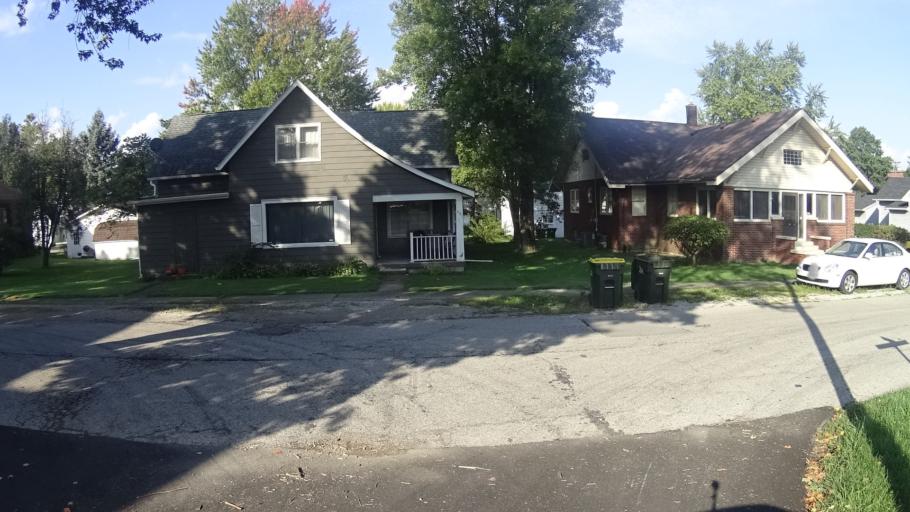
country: US
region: Indiana
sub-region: Madison County
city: Lapel
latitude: 40.0660
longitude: -85.8469
